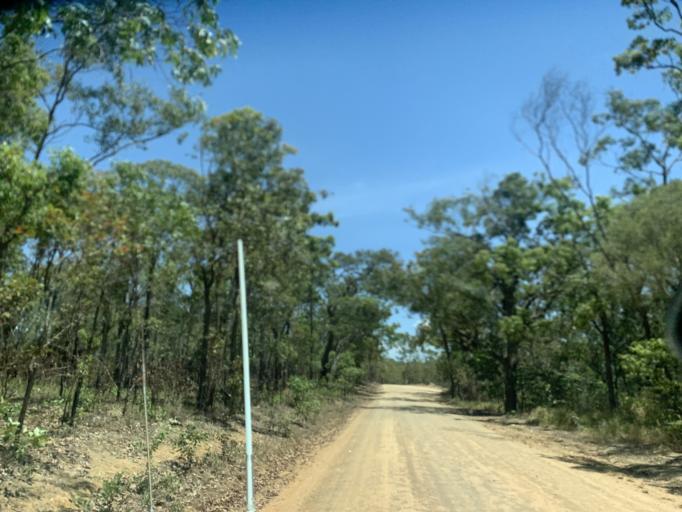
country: AU
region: Queensland
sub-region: Tablelands
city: Kuranda
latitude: -16.9220
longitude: 145.5905
